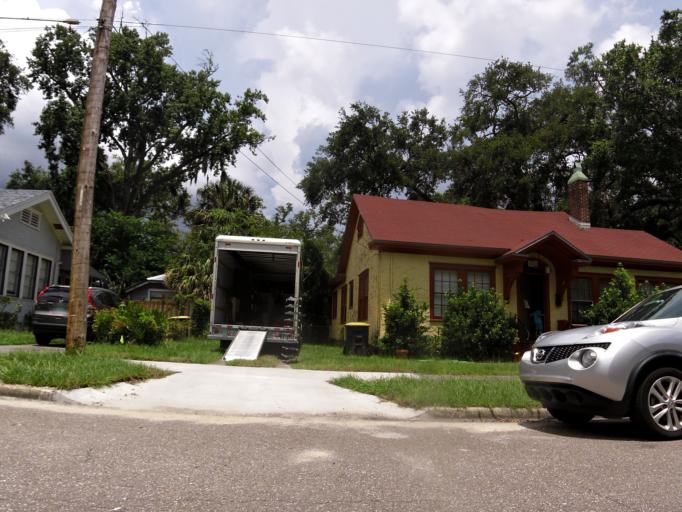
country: US
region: Florida
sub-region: Duval County
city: Jacksonville
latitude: 30.3046
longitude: -81.7007
